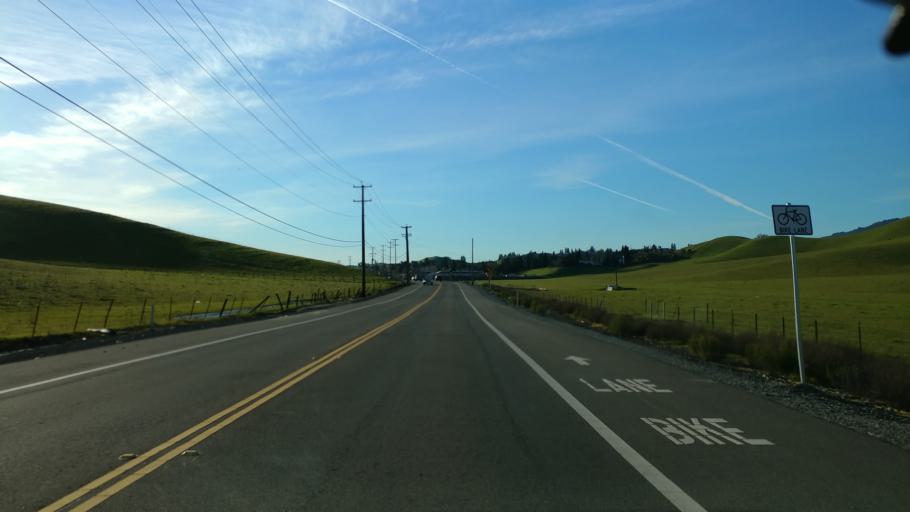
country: US
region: California
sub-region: Contra Costa County
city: Blackhawk
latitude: 37.7975
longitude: -121.8697
